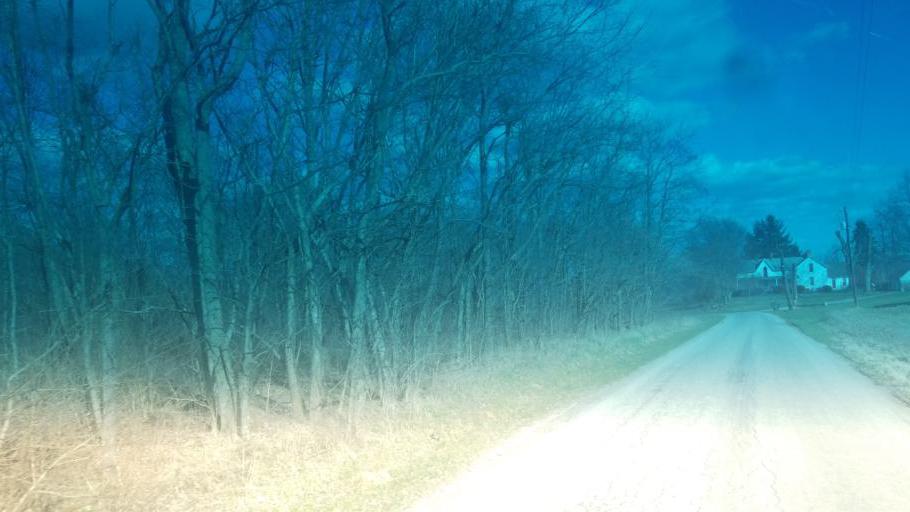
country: US
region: Ohio
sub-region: Highland County
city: Greenfield
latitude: 39.3004
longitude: -83.4380
